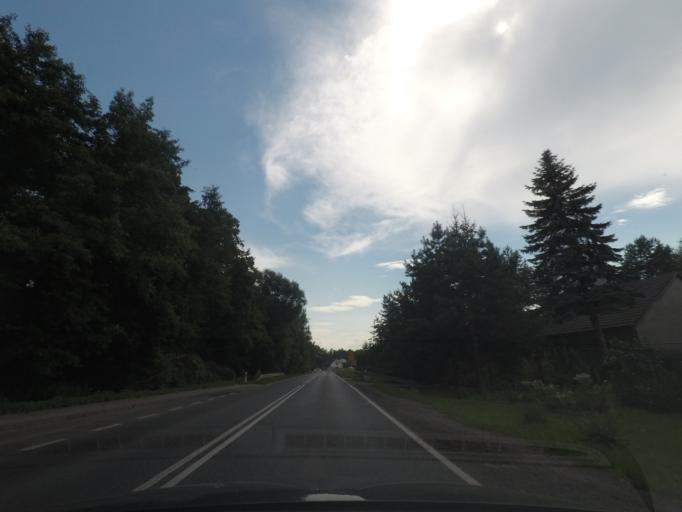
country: PL
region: Lesser Poland Voivodeship
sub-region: Powiat oswiecimski
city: Rajsko
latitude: 50.0008
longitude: 19.1745
